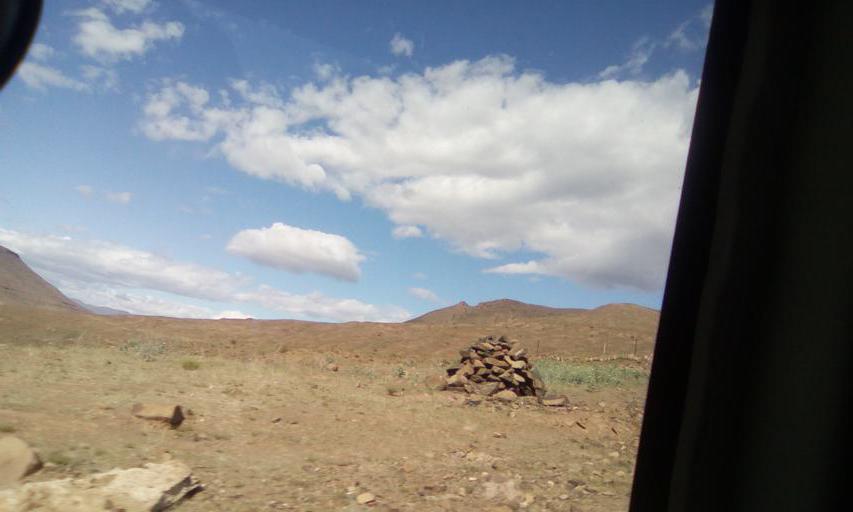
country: LS
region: Qacha's Nek
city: Qacha's Nek
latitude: -30.0259
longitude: 28.1773
